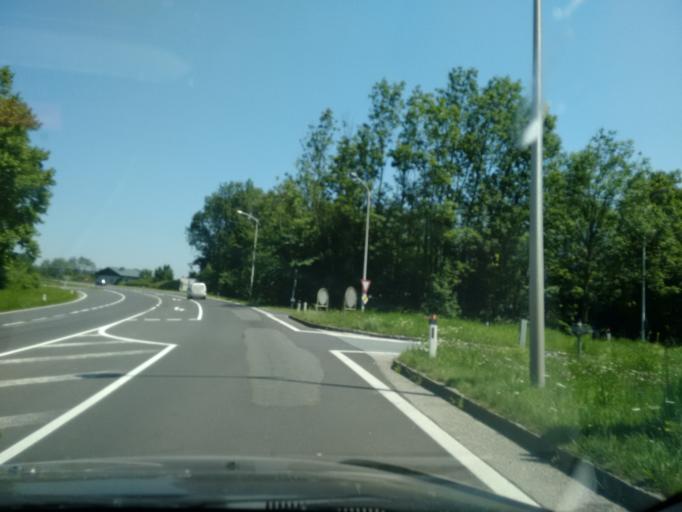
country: AT
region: Upper Austria
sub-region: Politischer Bezirk Gmunden
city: Altmunster
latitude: 47.9044
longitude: 13.7773
